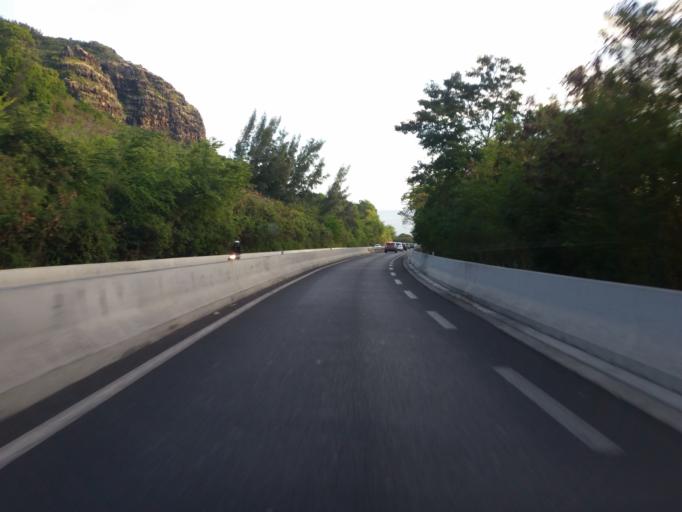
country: RE
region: Reunion
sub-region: Reunion
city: Saint-Denis
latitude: -20.8840
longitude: 55.4393
